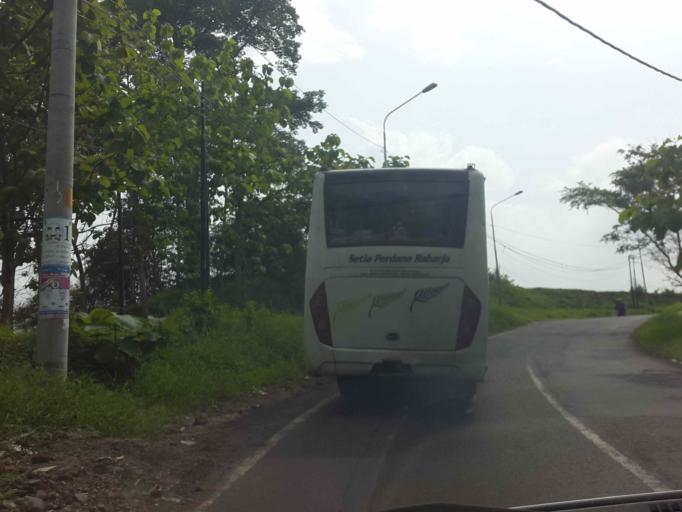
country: ID
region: Central Java
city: Semarang
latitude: -7.0599
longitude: 110.4504
